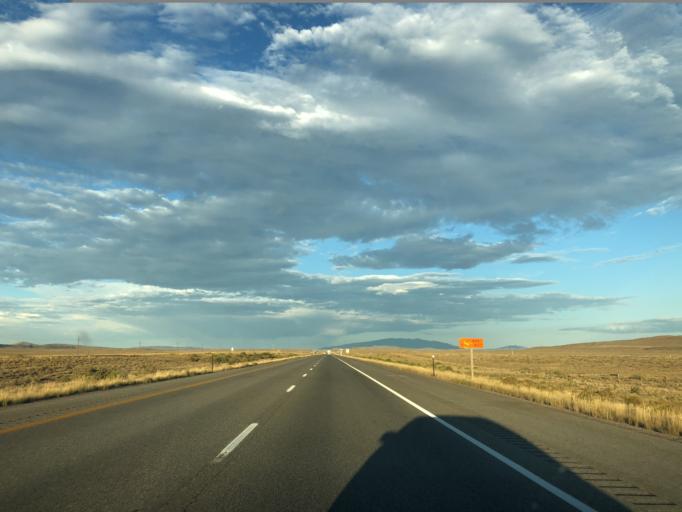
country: US
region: Wyoming
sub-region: Carbon County
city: Rawlins
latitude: 41.7625
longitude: -107.0096
